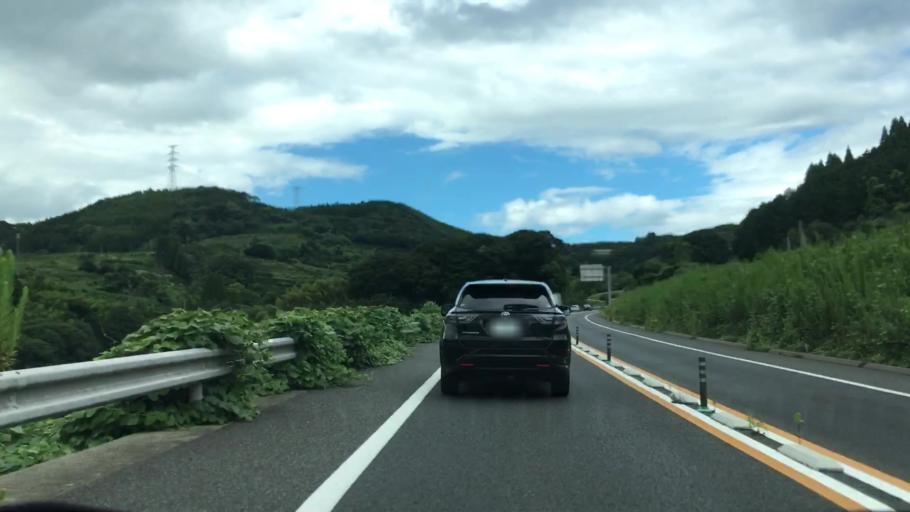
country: JP
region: Saga Prefecture
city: Karatsu
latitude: 33.3936
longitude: 129.9349
